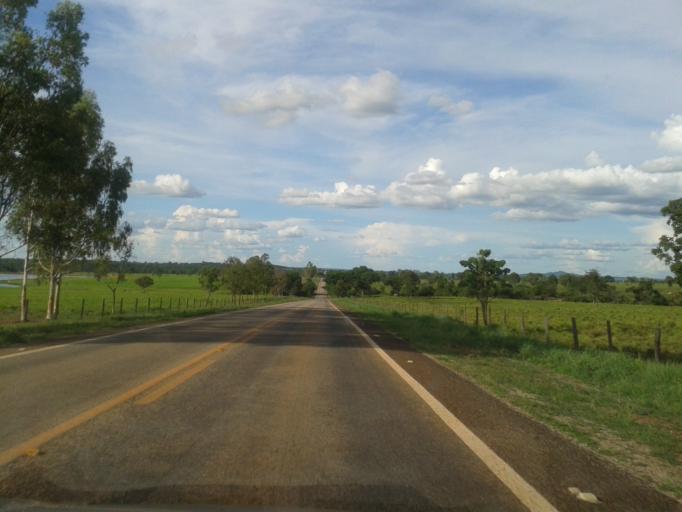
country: BR
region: Goias
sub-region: Crixas
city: Crixas
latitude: -14.2449
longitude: -50.3961
